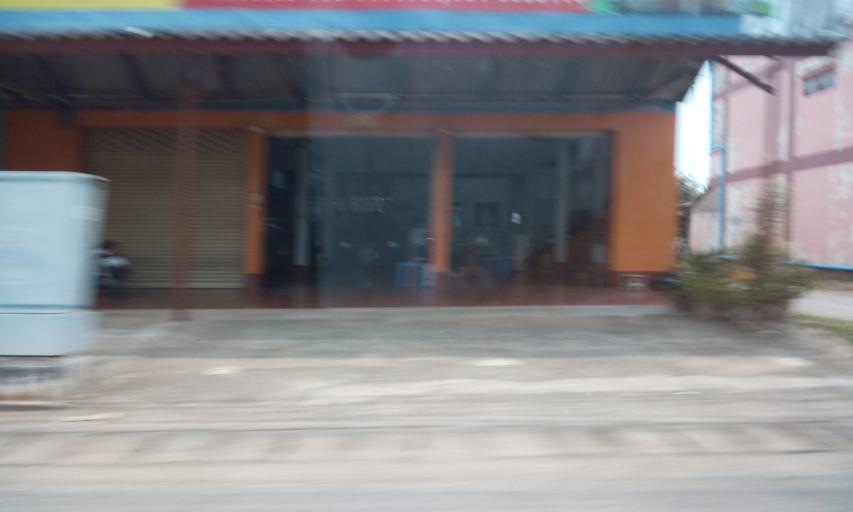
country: TH
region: Phayao
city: Chiang Kham
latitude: 19.5235
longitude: 100.3055
